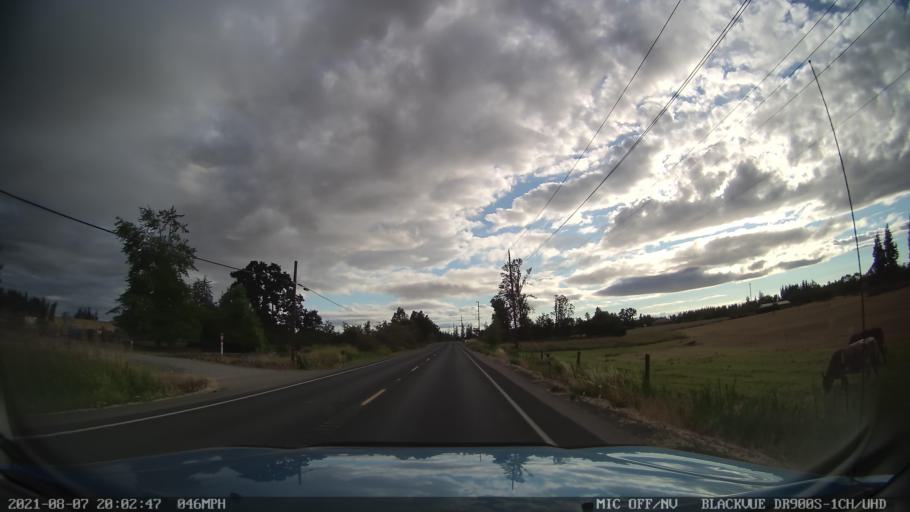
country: US
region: Oregon
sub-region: Marion County
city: Silverton
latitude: 45.0009
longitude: -122.8083
